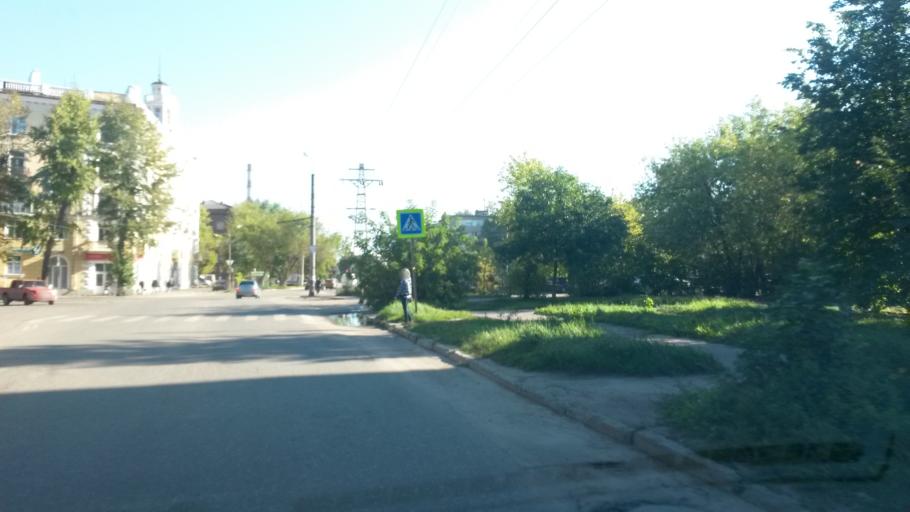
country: RU
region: Ivanovo
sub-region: Gorod Ivanovo
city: Ivanovo
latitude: 56.9998
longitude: 40.9606
